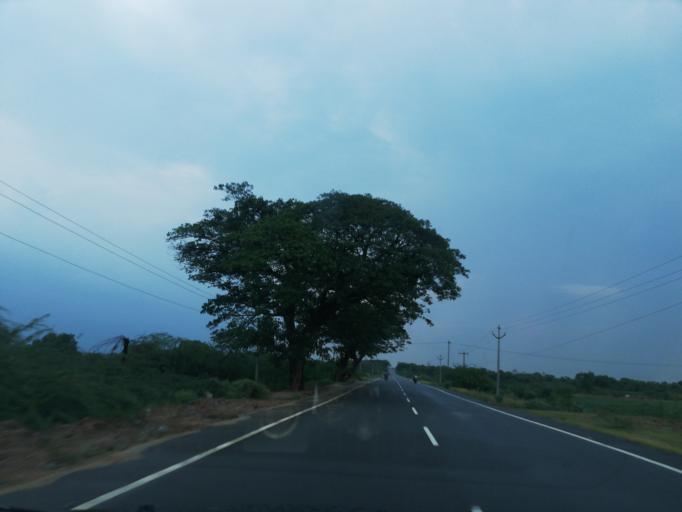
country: IN
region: Andhra Pradesh
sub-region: Guntur
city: Macherla
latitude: 16.6787
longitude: 79.2630
